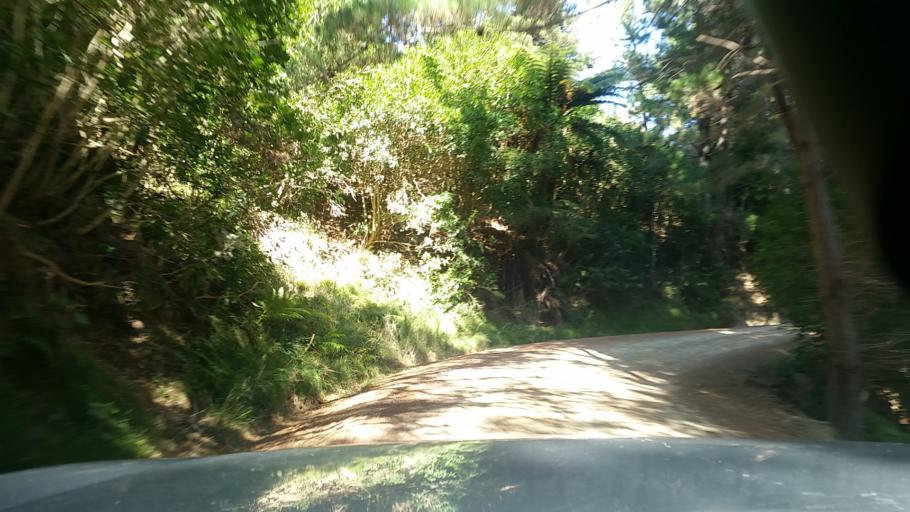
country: NZ
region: Marlborough
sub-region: Marlborough District
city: Picton
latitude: -41.2985
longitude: 174.1811
